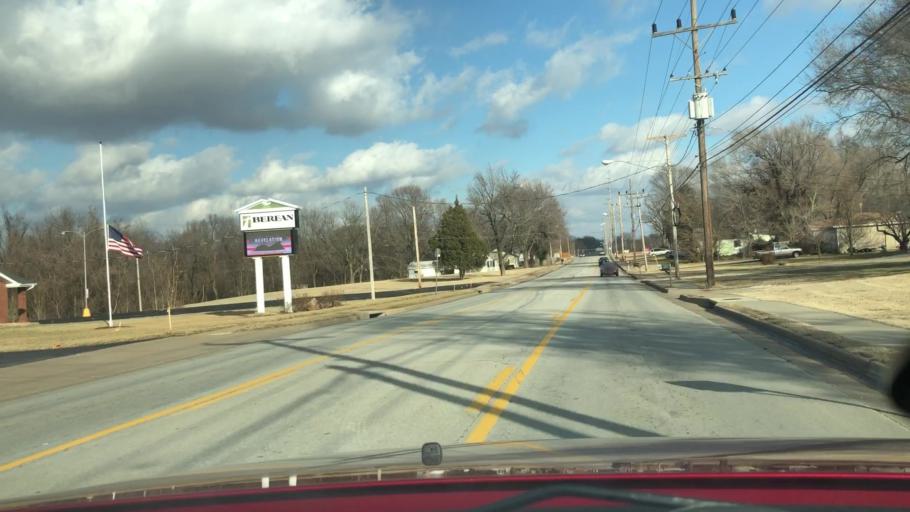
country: US
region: Missouri
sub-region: Greene County
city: Springfield
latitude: 37.2516
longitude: -93.2867
